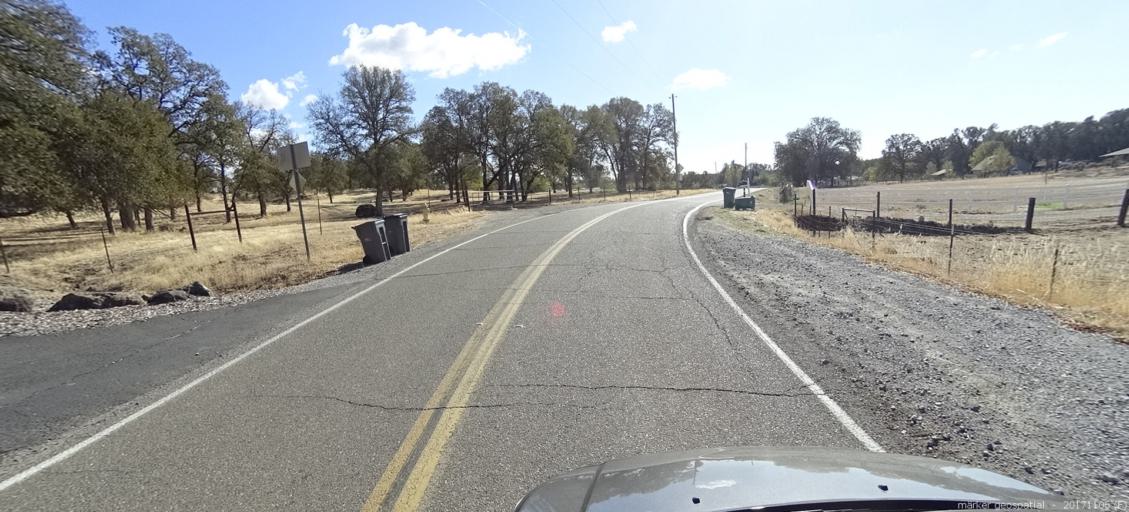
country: US
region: California
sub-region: Shasta County
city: Palo Cedro
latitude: 40.5794
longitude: -122.2200
